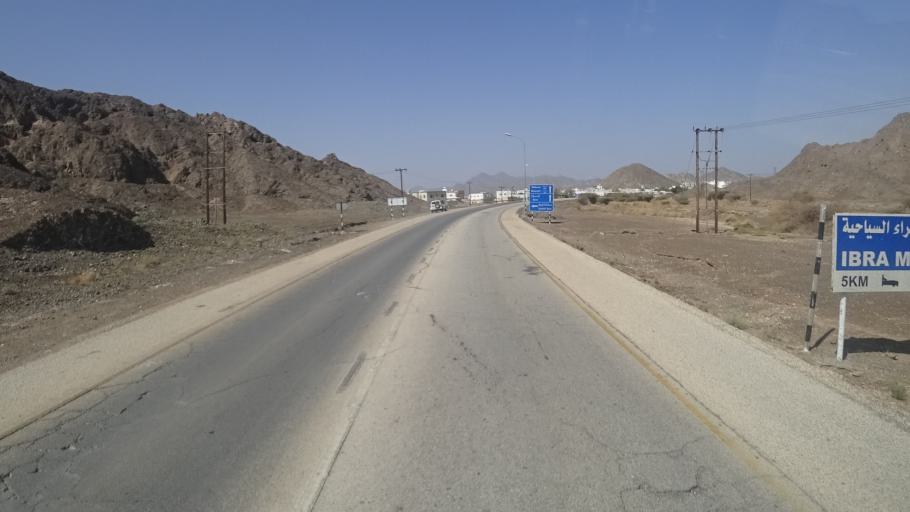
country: OM
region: Ash Sharqiyah
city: Ibra'
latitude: 22.6834
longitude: 58.5590
